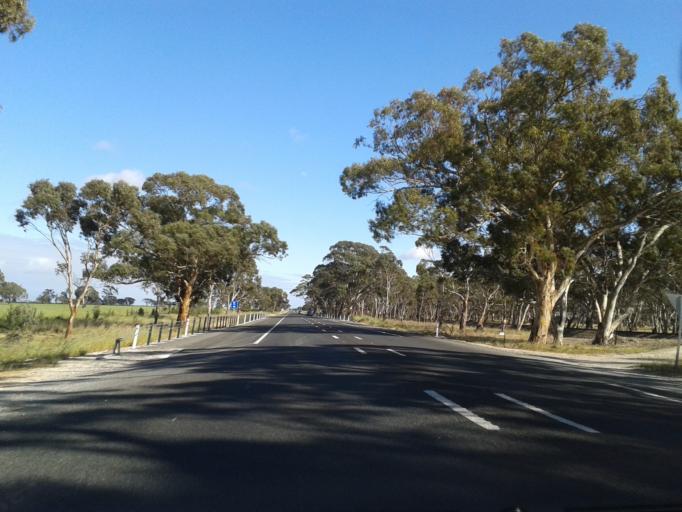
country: AU
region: South Australia
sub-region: Tatiara
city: Bordertown
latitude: -36.2652
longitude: 140.6971
